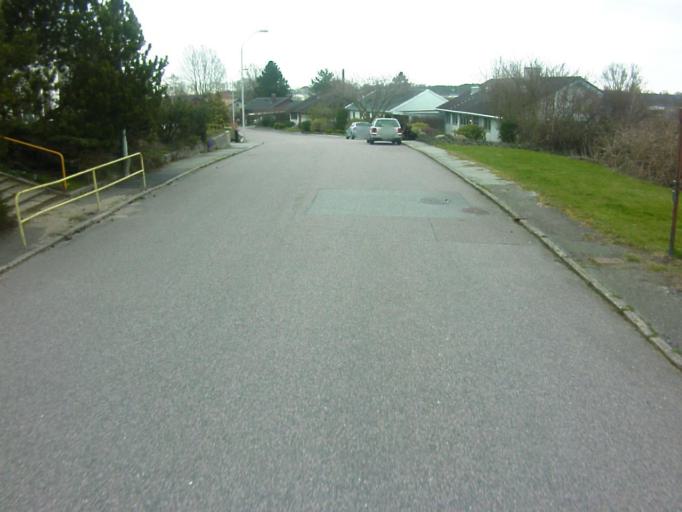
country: SE
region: Skane
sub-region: Kavlinge Kommun
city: Kaevlinge
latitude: 55.7880
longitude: 13.0914
